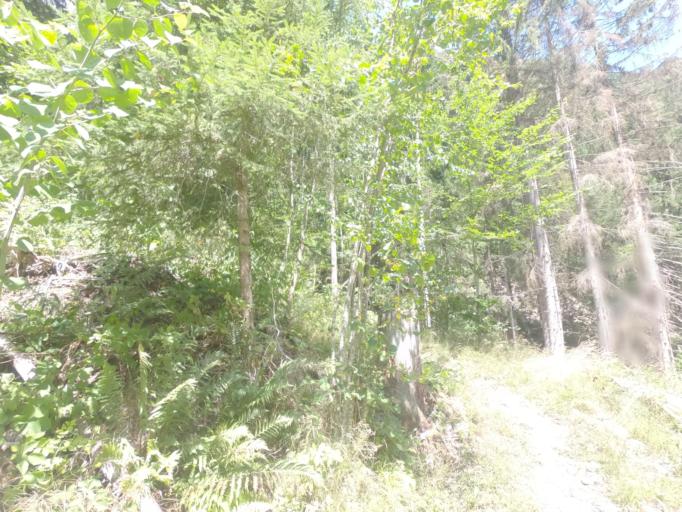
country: CH
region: Valais
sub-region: Saint-Maurice District
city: Salvan
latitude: 46.0786
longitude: 6.9752
